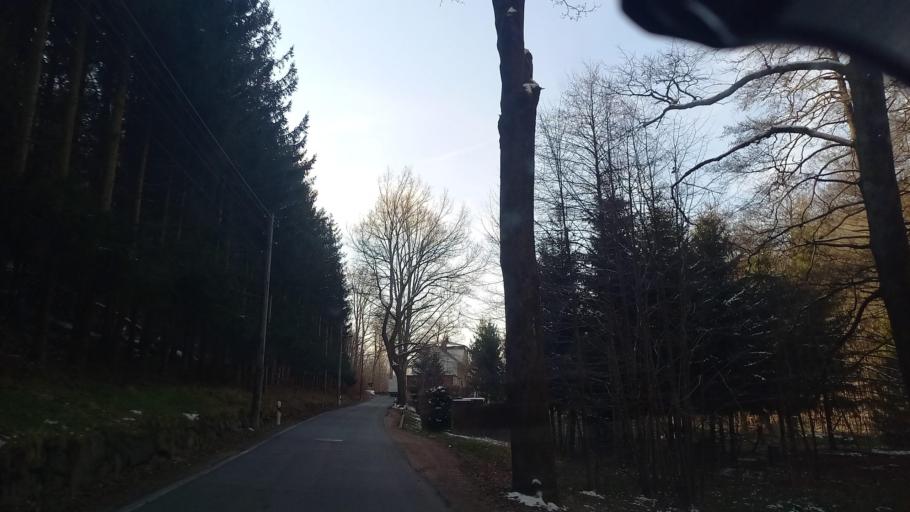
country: DE
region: Saxony
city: Kirchberg
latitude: 50.5830
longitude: 12.4921
